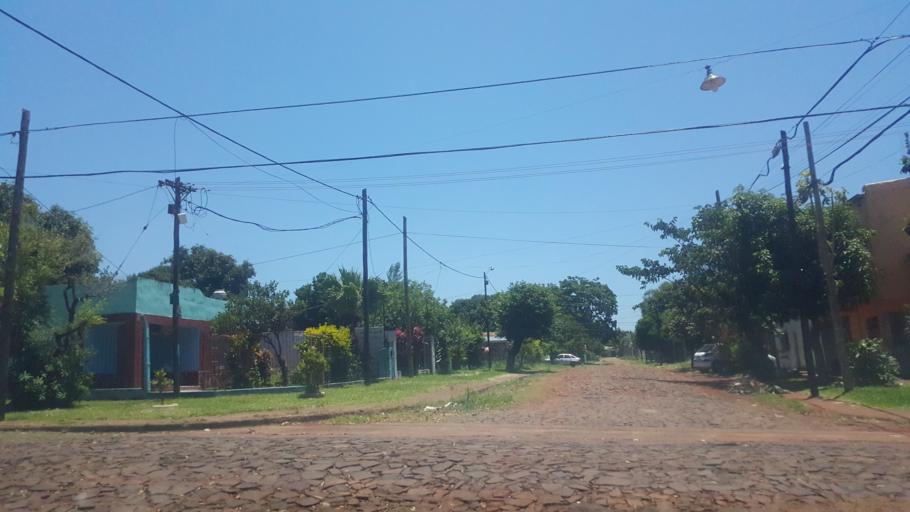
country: AR
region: Misiones
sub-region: Departamento de Capital
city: Posadas
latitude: -27.3734
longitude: -55.9144
